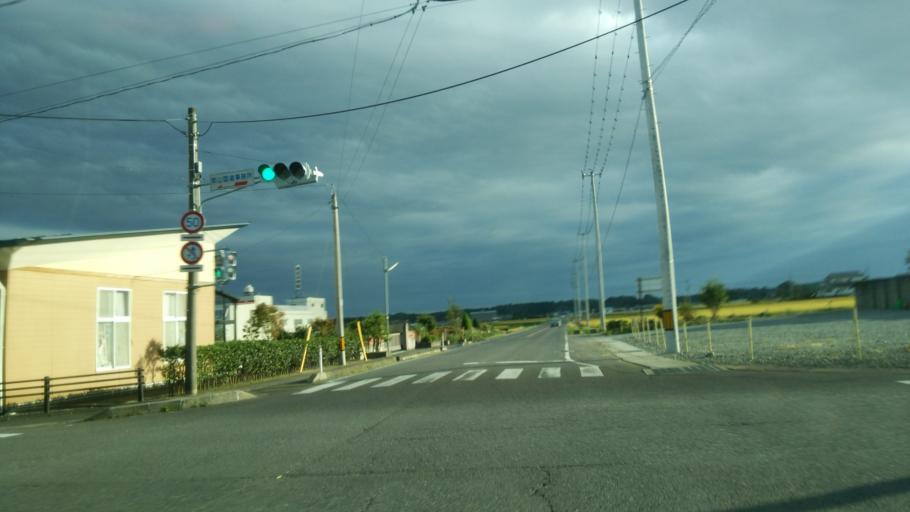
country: JP
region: Fukushima
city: Koriyama
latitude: 37.3740
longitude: 140.3411
